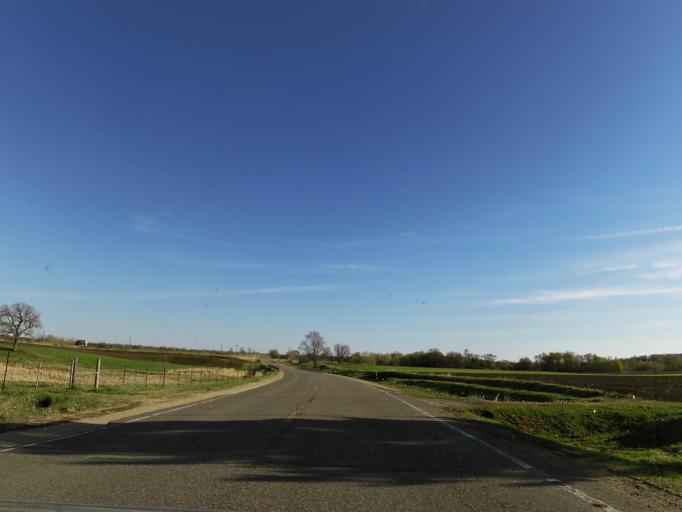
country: US
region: Minnesota
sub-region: Dakota County
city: Lakeville
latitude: 44.6162
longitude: -93.2633
